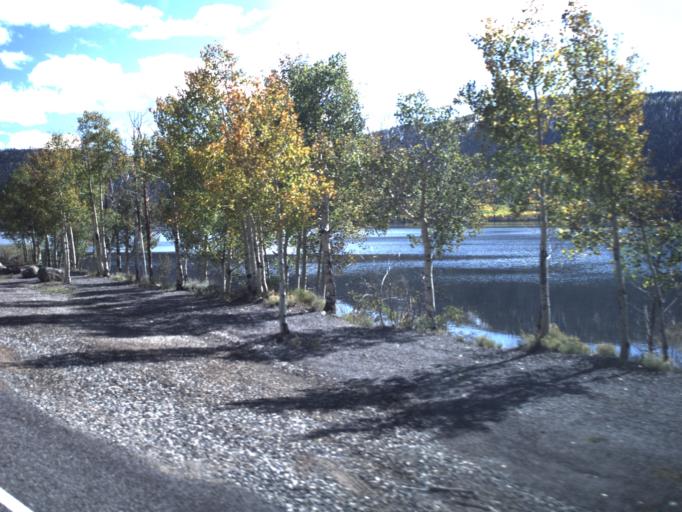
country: US
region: Utah
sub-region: Wayne County
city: Loa
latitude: 38.5578
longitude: -111.7125
